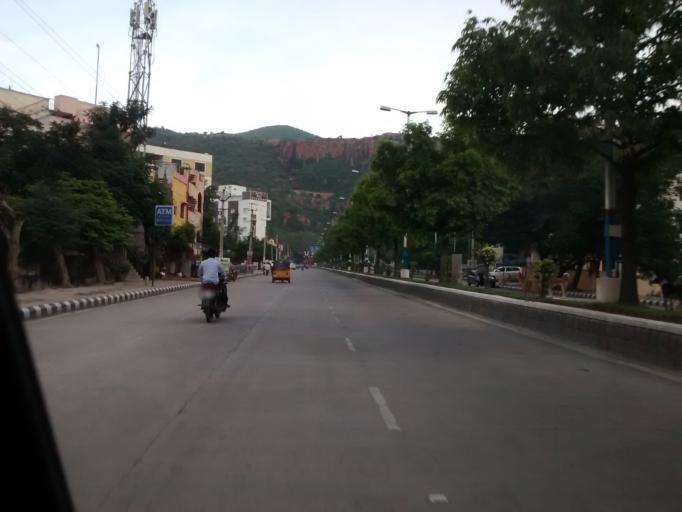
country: IN
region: Andhra Pradesh
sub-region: Chittoor
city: Akkarampalle
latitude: 13.6512
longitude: 79.4228
